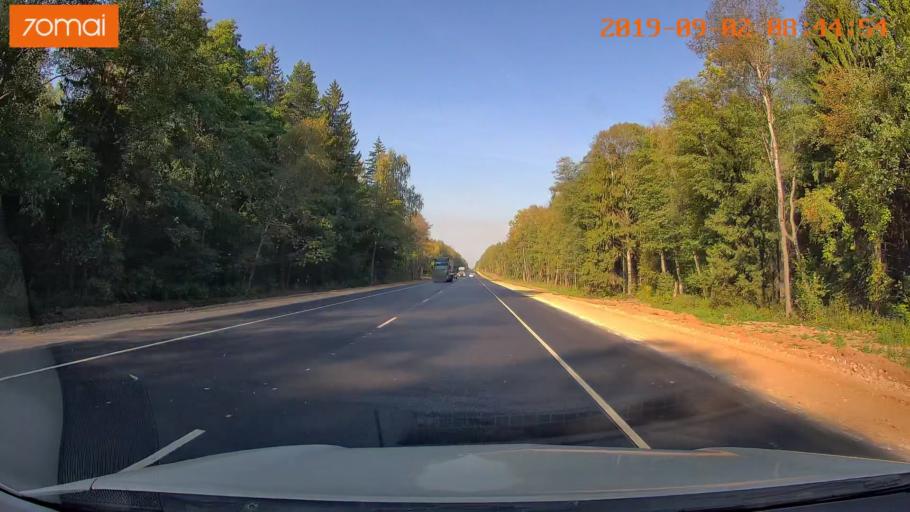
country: RU
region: Kaluga
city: Medyn'
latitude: 54.9702
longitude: 36.0210
